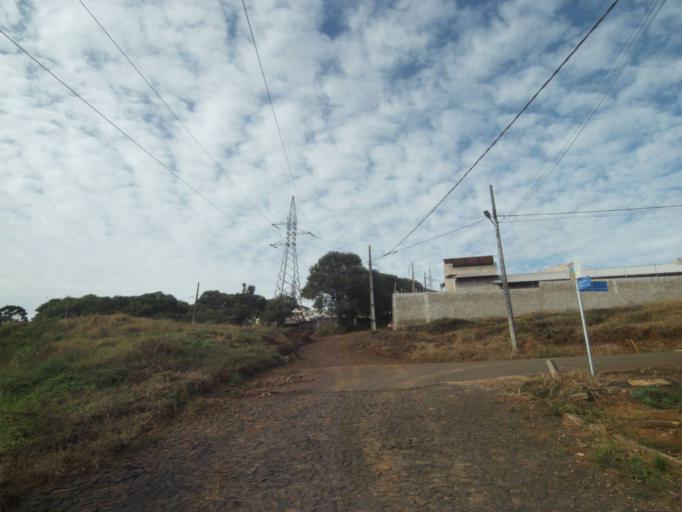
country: BR
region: Parana
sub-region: Telemaco Borba
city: Telemaco Borba
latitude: -24.3380
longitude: -50.6088
